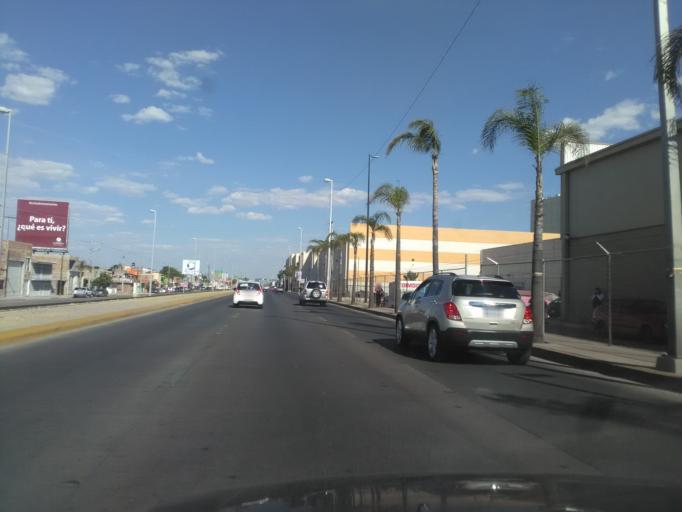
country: MX
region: Durango
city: Victoria de Durango
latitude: 24.0371
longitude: -104.6527
